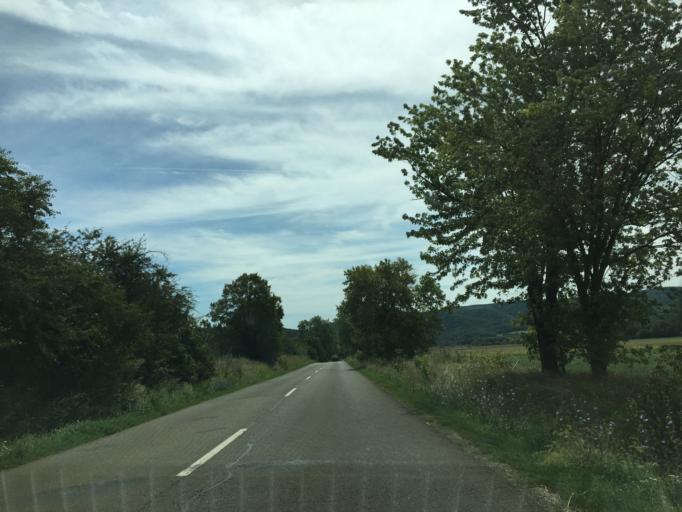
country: HU
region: Komarom-Esztergom
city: Esztergom
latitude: 47.8800
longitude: 18.7803
